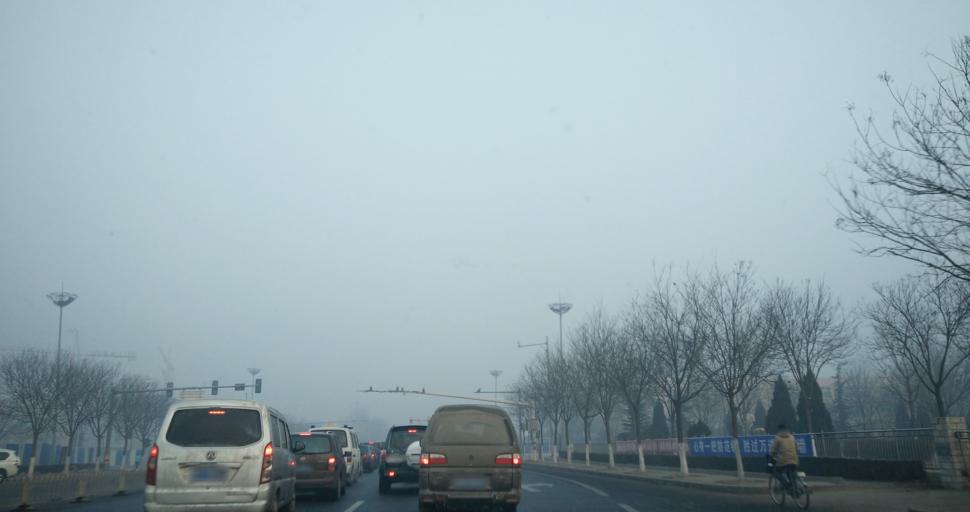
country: CN
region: Beijing
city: Yinghai
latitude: 39.7635
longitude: 116.4421
